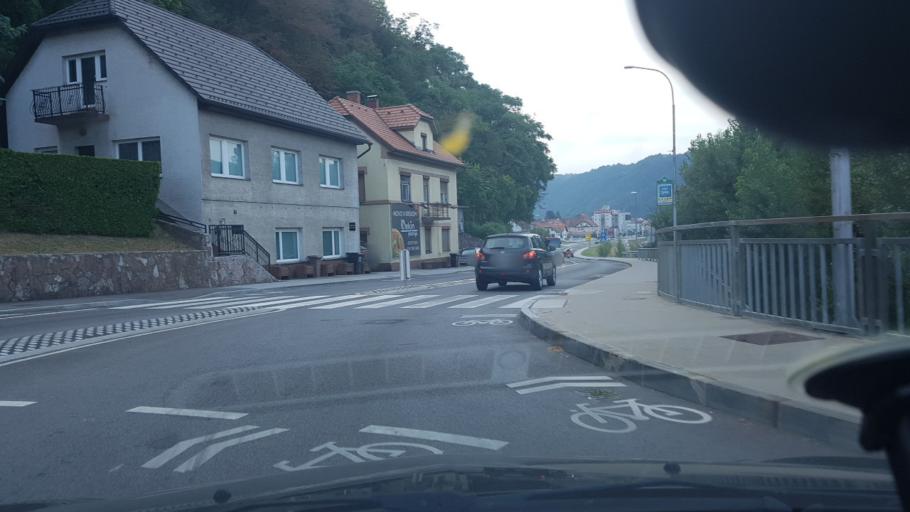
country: SI
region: Krsko
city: Krsko
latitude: 45.9567
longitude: 15.4866
